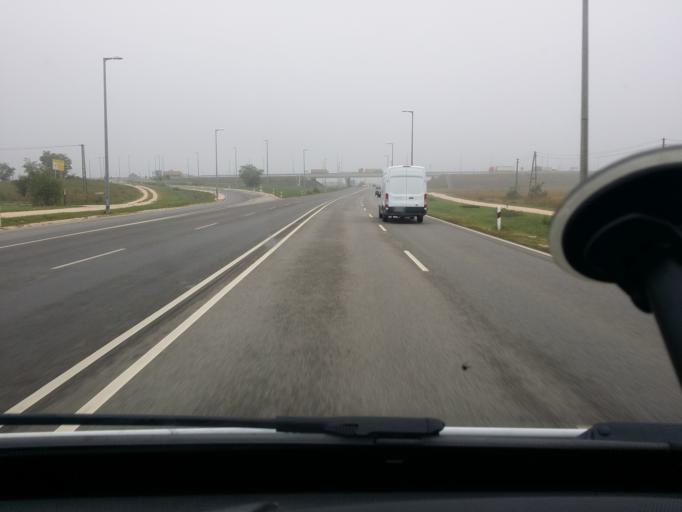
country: HU
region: Bacs-Kiskun
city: Kecskemet
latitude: 46.9431
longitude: 19.6564
